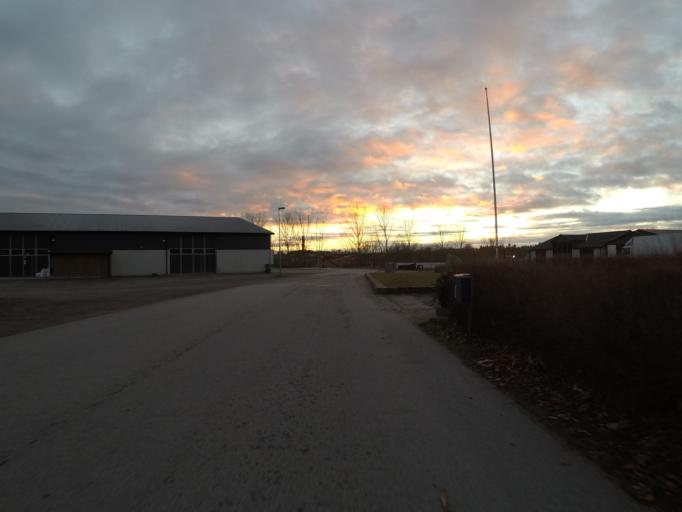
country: SE
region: Skane
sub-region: Sjobo Kommun
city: Sjoebo
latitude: 55.6436
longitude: 13.6919
